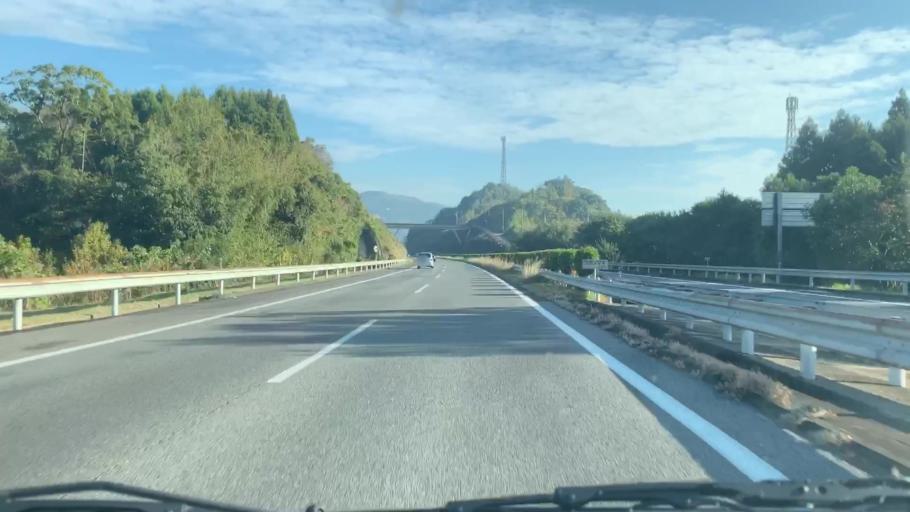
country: JP
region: Saga Prefecture
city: Takeocho-takeo
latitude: 33.2764
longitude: 130.1149
